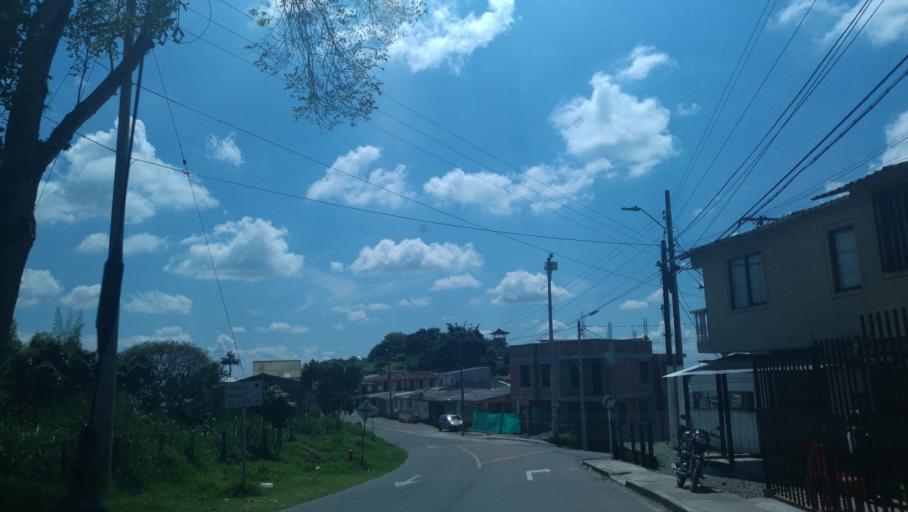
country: CO
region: Quindio
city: Circasia
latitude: 4.6213
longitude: -75.6304
